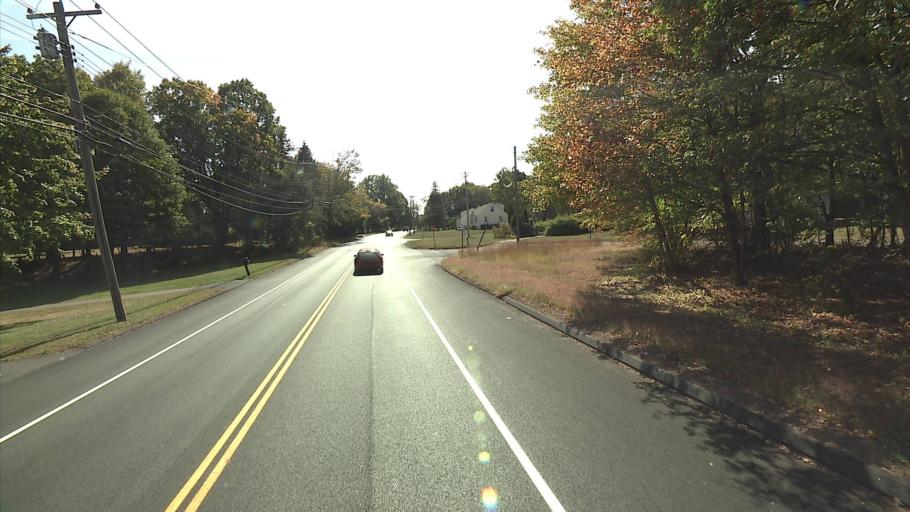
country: US
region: Connecticut
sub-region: New Haven County
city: North Haven
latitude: 41.3653
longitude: -72.8531
